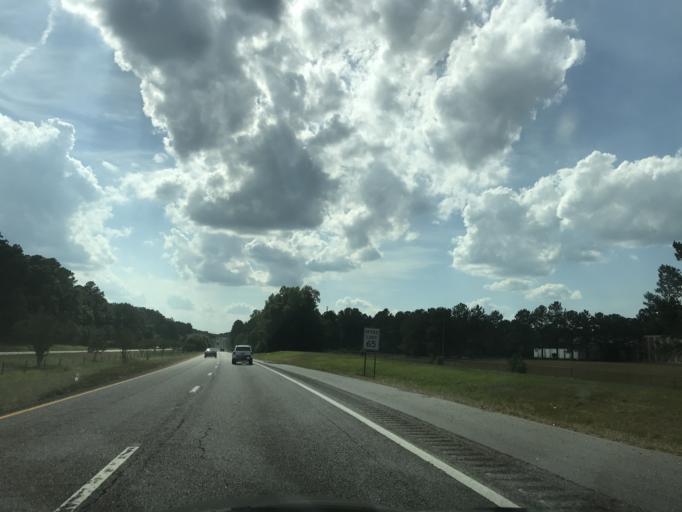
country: US
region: North Carolina
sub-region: Nash County
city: Red Oak
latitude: 35.9806
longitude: -77.8571
